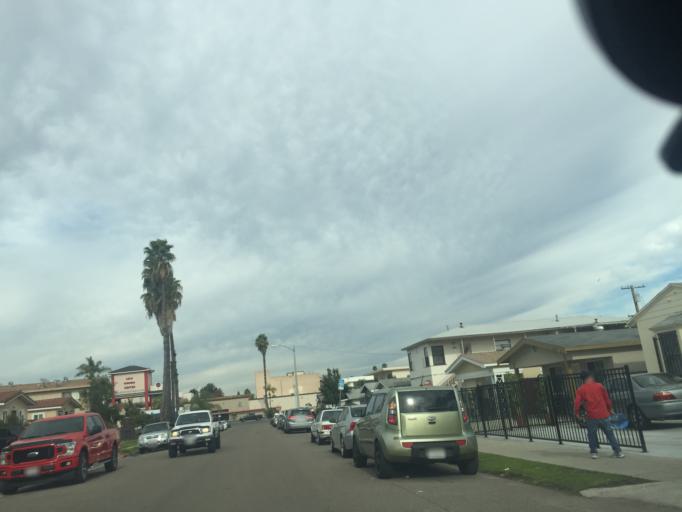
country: US
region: California
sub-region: San Diego County
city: Lemon Grove
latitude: 32.7545
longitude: -117.0932
